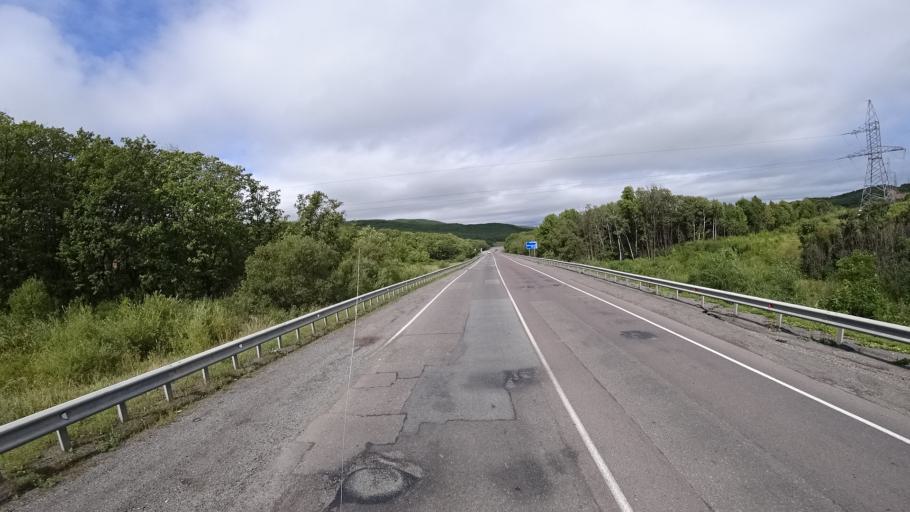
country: RU
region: Primorskiy
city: Lyalichi
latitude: 44.1339
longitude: 132.4274
